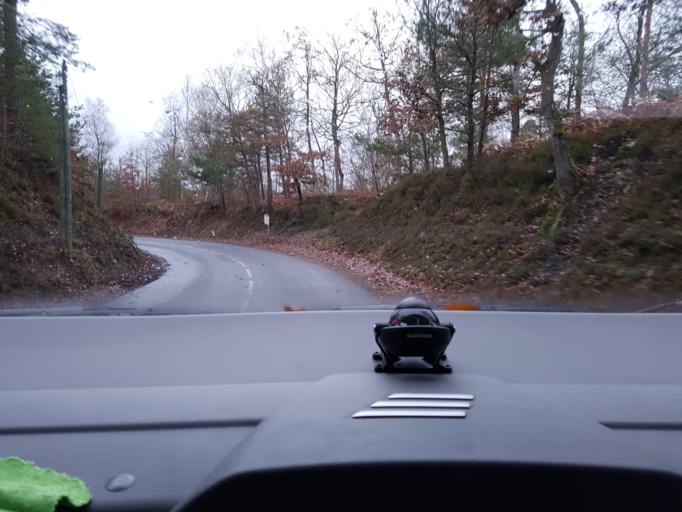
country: FR
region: Haute-Normandie
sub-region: Departement de l'Eure
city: Beaumont-le-Roger
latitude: 49.0677
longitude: 0.7702
